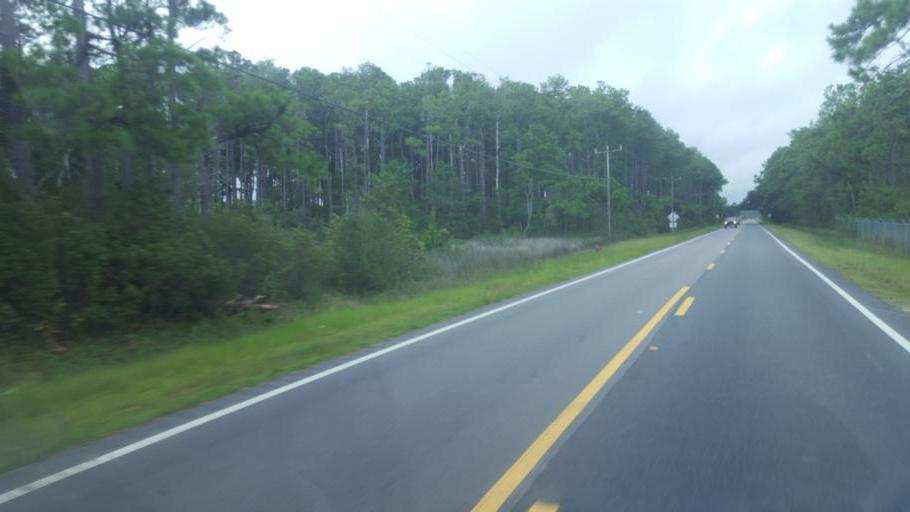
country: US
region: North Carolina
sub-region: Dare County
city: Wanchese
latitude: 35.8651
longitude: -75.6487
